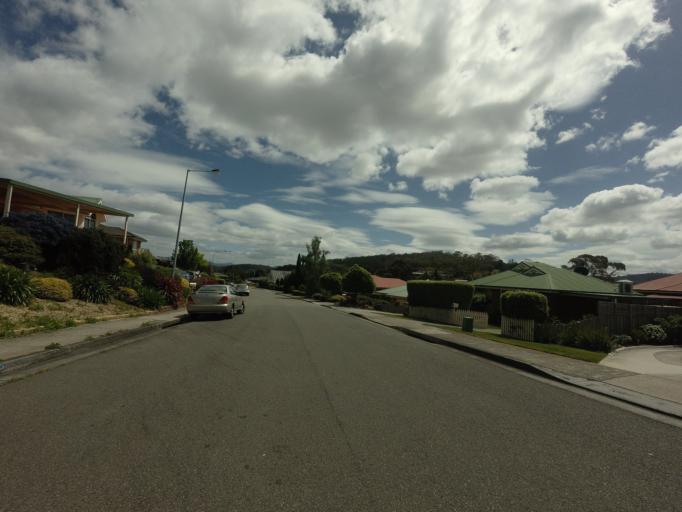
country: AU
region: Tasmania
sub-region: Clarence
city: Howrah
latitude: -42.8893
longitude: 147.4218
